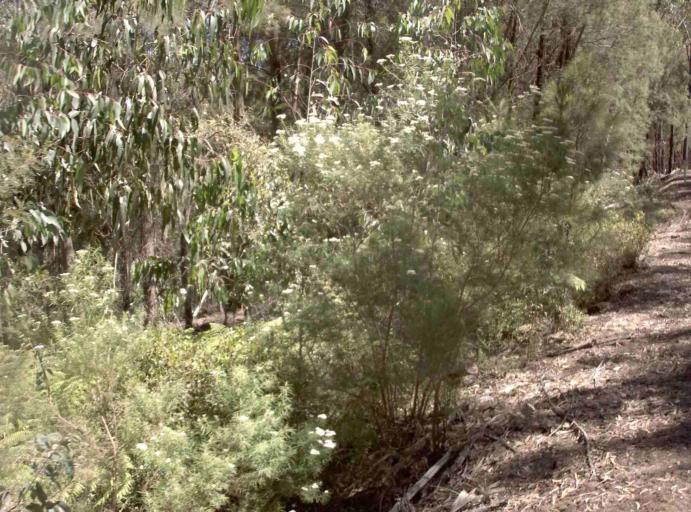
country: AU
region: Victoria
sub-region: East Gippsland
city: Lakes Entrance
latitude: -37.3758
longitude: 148.2175
